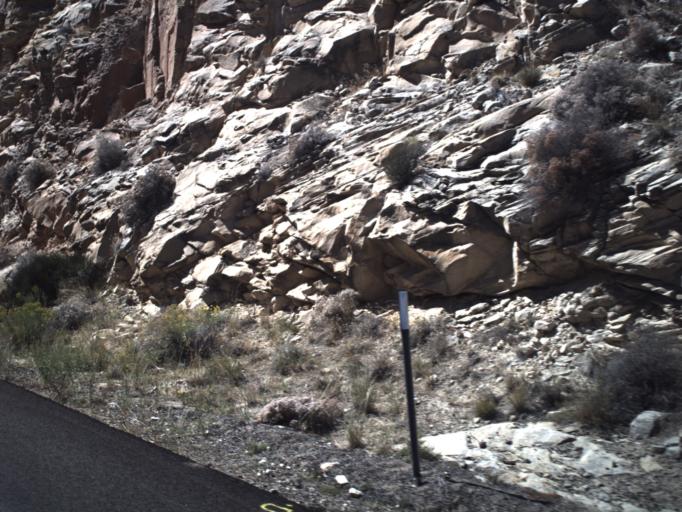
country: US
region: Utah
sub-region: Wayne County
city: Loa
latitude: 37.7981
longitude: -111.4079
